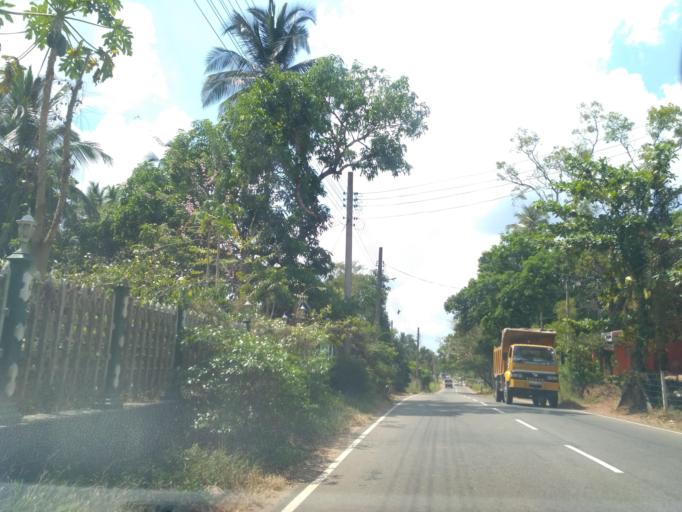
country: LK
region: North Western
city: Kuliyapitiya
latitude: 7.3266
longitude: 80.0610
